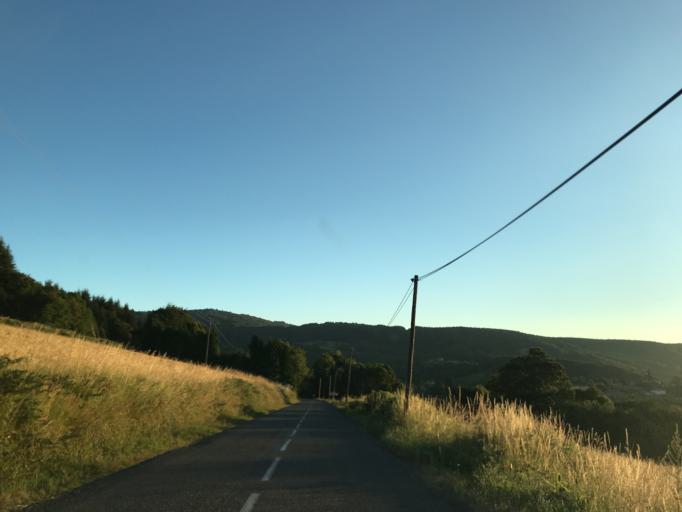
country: FR
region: Auvergne
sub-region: Departement du Puy-de-Dome
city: Chabreloche
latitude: 45.8301
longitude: 3.6866
